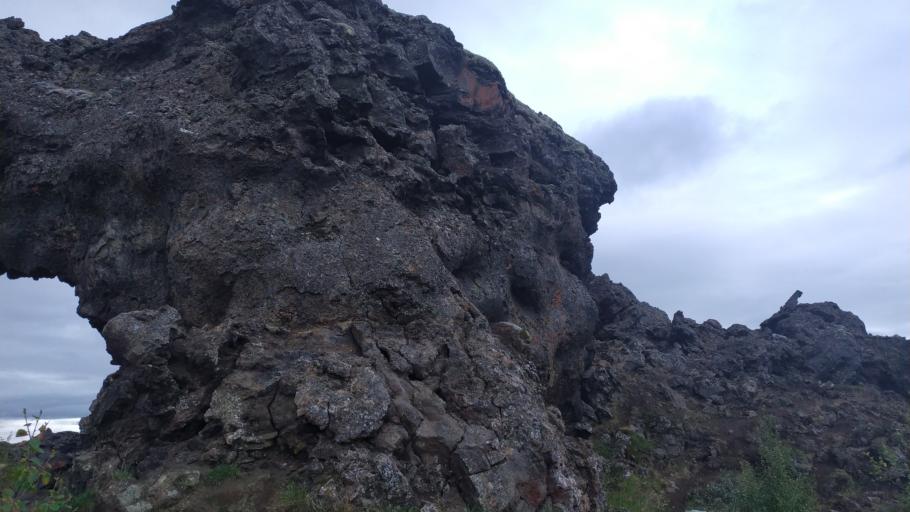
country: IS
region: Northeast
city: Laugar
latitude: 65.5903
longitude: -16.9043
